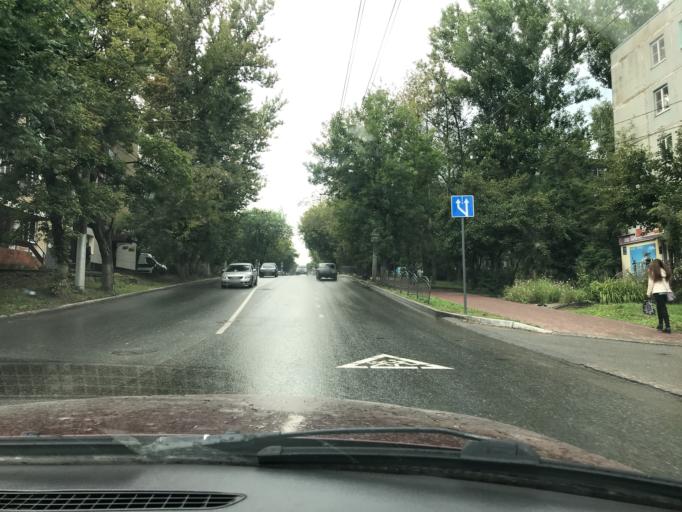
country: RU
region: Kaluga
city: Kaluga
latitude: 54.5143
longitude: 36.2823
